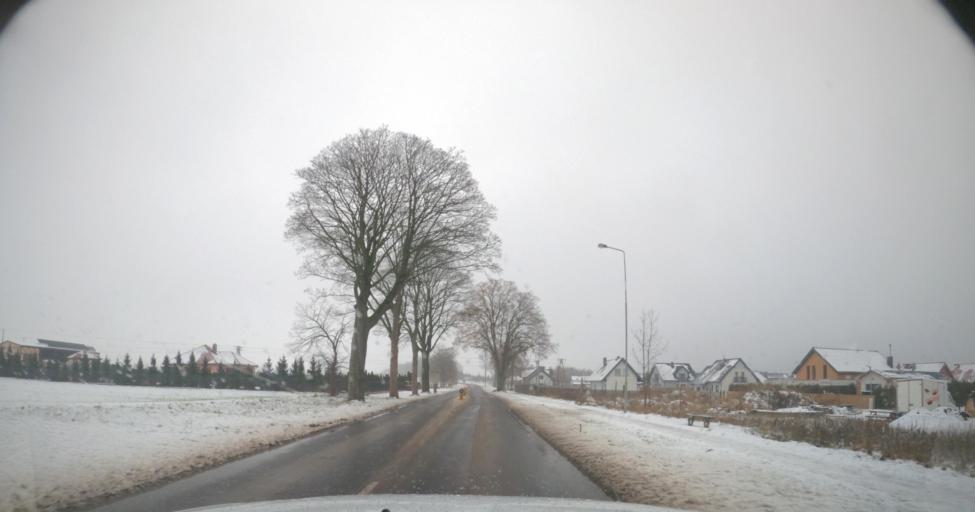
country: PL
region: West Pomeranian Voivodeship
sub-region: Powiat gryficki
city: Gryfice
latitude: 53.9121
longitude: 15.2199
